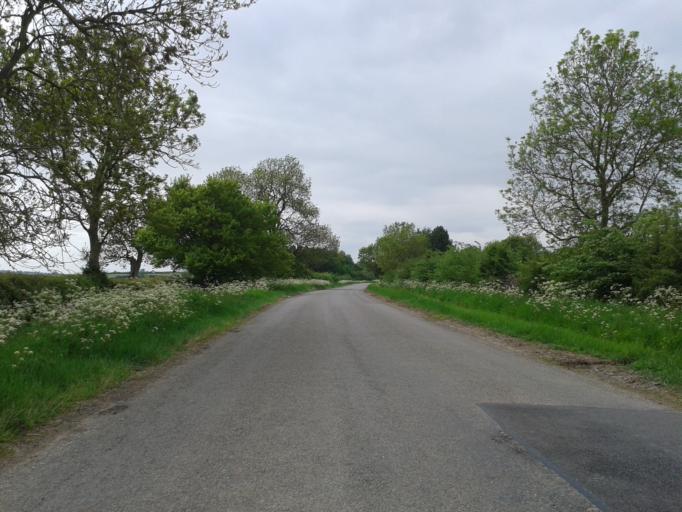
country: GB
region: England
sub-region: Leicestershire
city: Market Harborough
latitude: 52.5251
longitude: -0.8848
